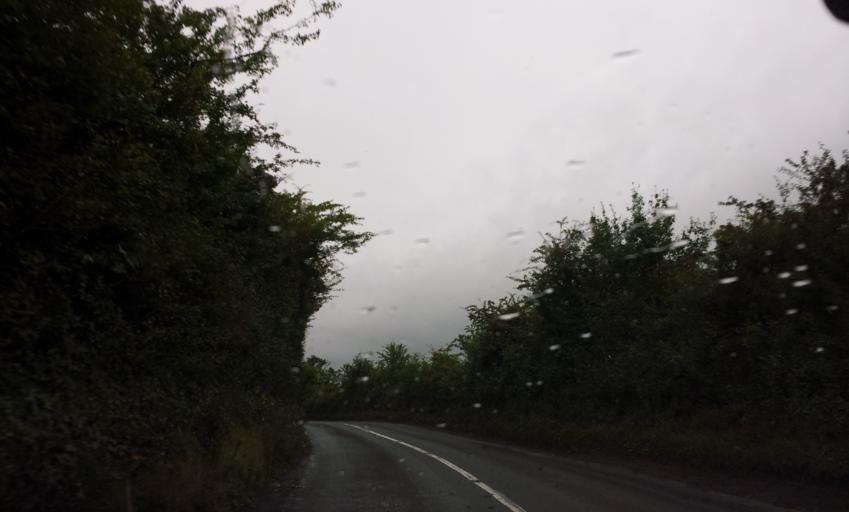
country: IE
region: Munster
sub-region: County Cork
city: Mallow
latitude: 52.2371
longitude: -8.4878
